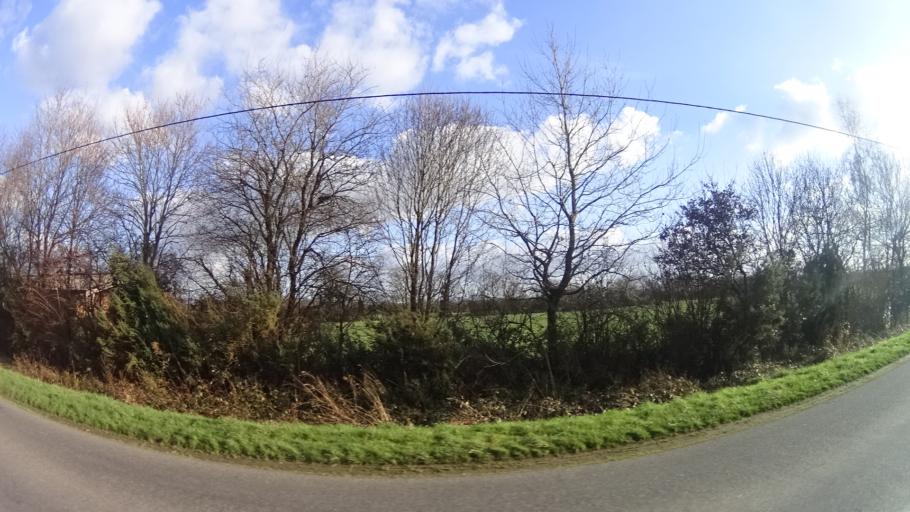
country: FR
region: Pays de la Loire
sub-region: Departement de la Loire-Atlantique
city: Guemene-Penfao
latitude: 47.5960
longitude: -1.8490
